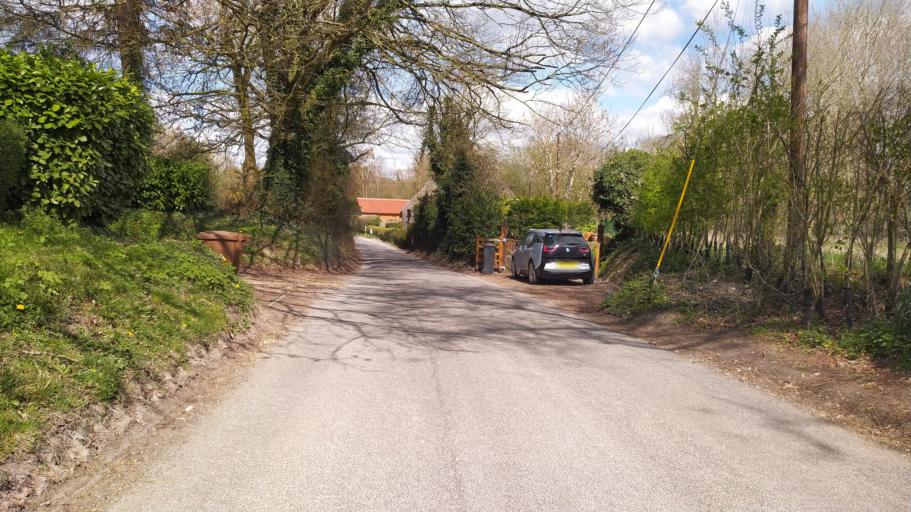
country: GB
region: England
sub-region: Hampshire
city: Abbotts Ann
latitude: 51.2073
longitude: -1.5753
